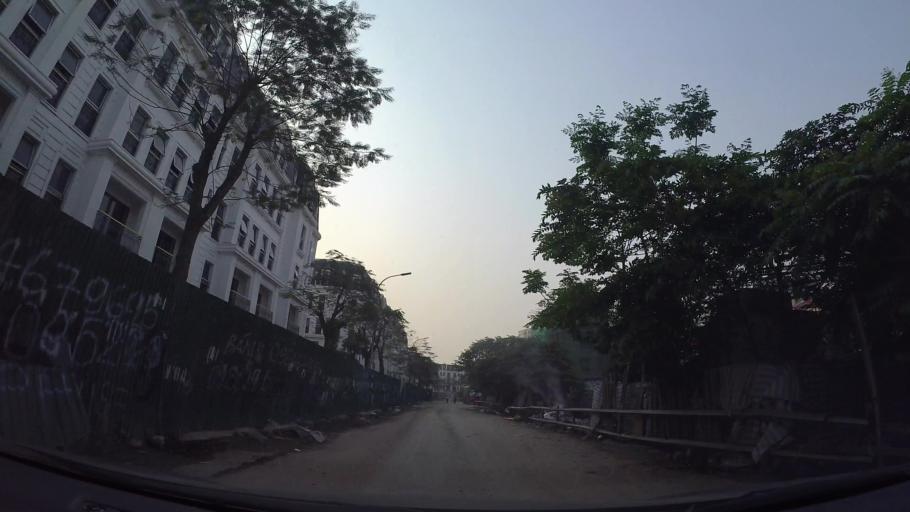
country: VN
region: Ha Noi
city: Thanh Xuan
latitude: 20.9782
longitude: 105.8149
